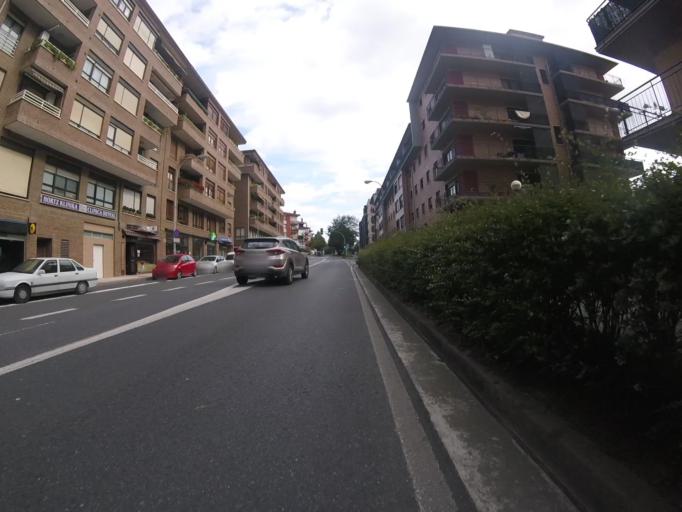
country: ES
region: Basque Country
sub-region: Provincia de Guipuzcoa
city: Urnieta
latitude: 43.2495
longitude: -1.9916
